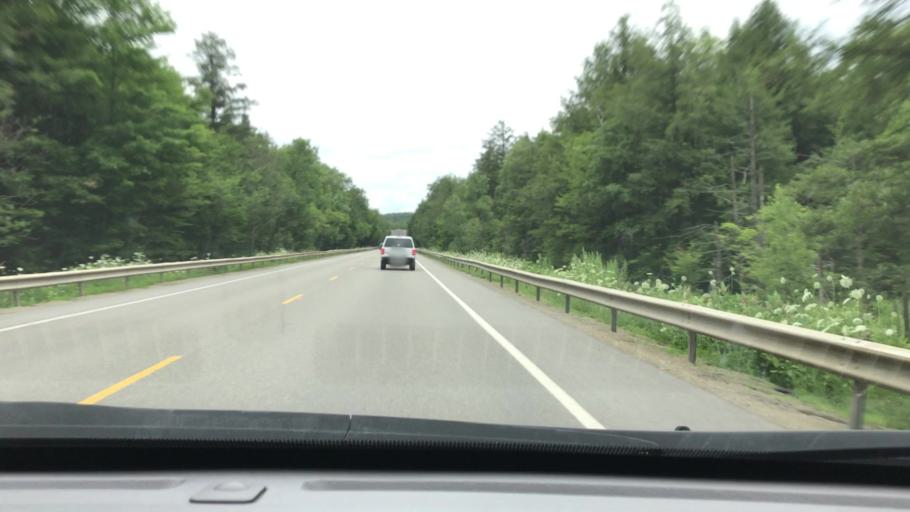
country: US
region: Pennsylvania
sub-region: McKean County
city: Kane
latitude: 41.6810
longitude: -78.6871
